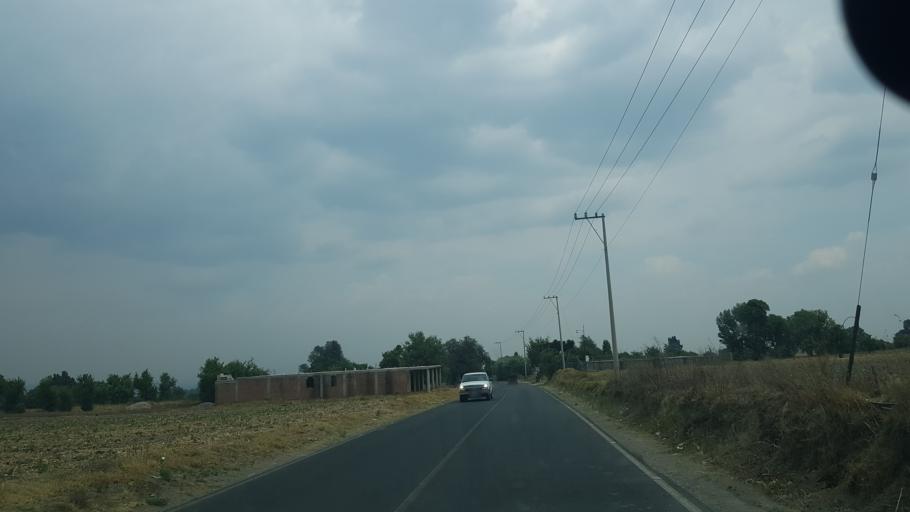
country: MX
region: Puebla
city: San Lorenzo Chiautzingo
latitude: 19.1983
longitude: -98.4521
